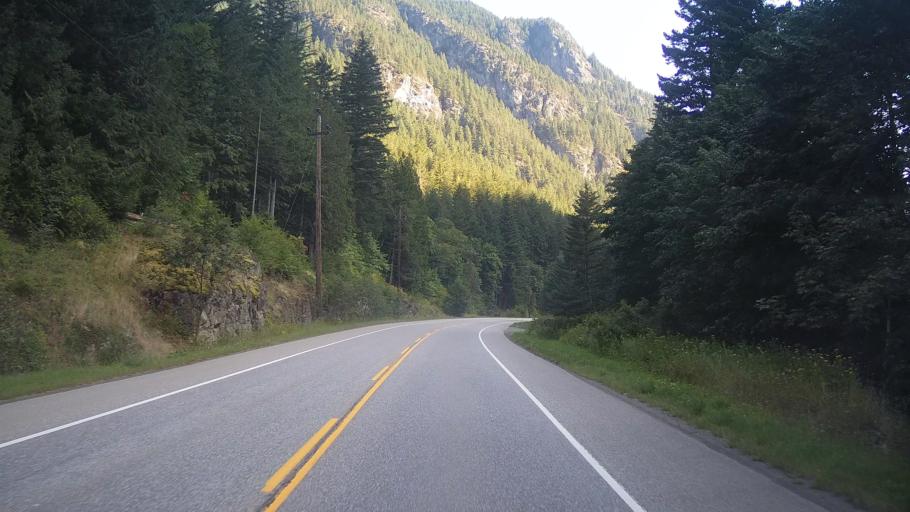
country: CA
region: British Columbia
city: Hope
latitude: 49.6082
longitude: -121.4154
